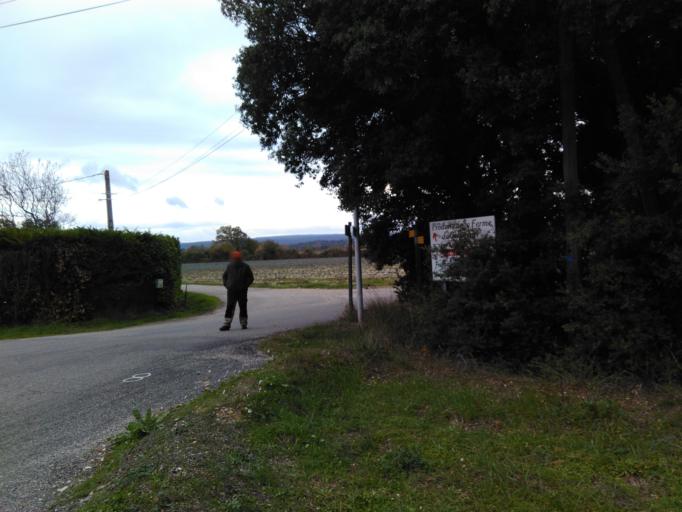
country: FR
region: Provence-Alpes-Cote d'Azur
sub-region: Departement du Vaucluse
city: Grillon
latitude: 44.3771
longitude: 4.9178
